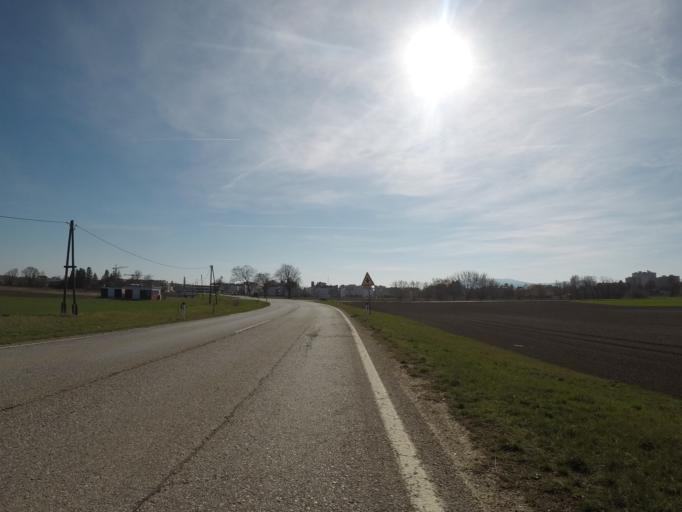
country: AT
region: Lower Austria
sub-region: Politischer Bezirk Modling
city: Vosendorf
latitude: 48.1206
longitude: 16.3527
